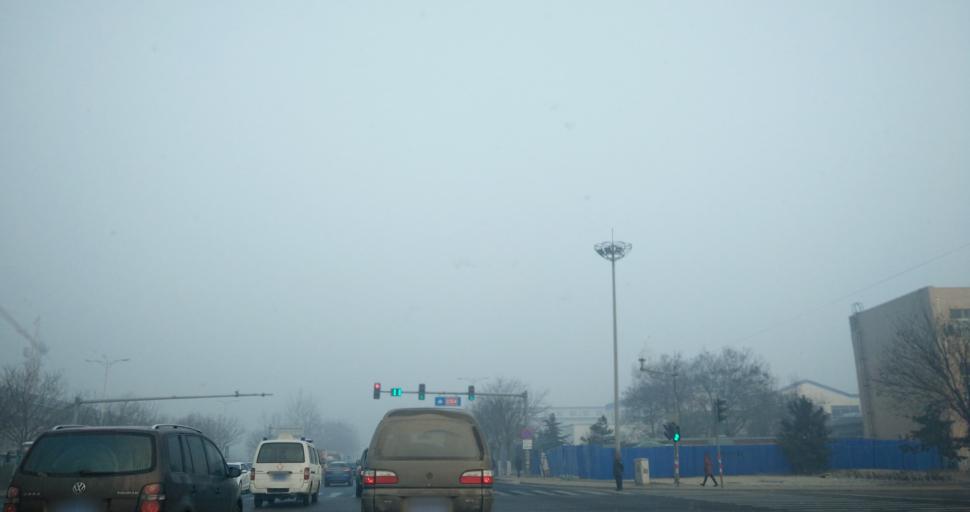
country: CN
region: Beijing
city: Yinghai
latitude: 39.7642
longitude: 116.4419
